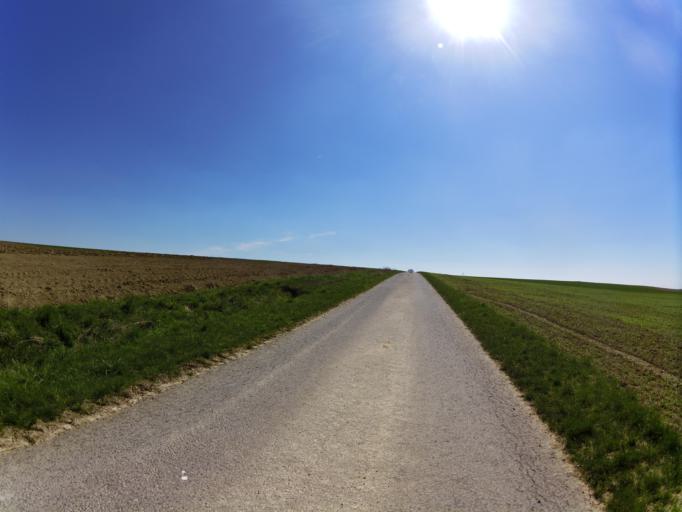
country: DE
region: Bavaria
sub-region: Regierungsbezirk Unterfranken
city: Winterhausen
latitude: 49.6889
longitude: 9.9997
